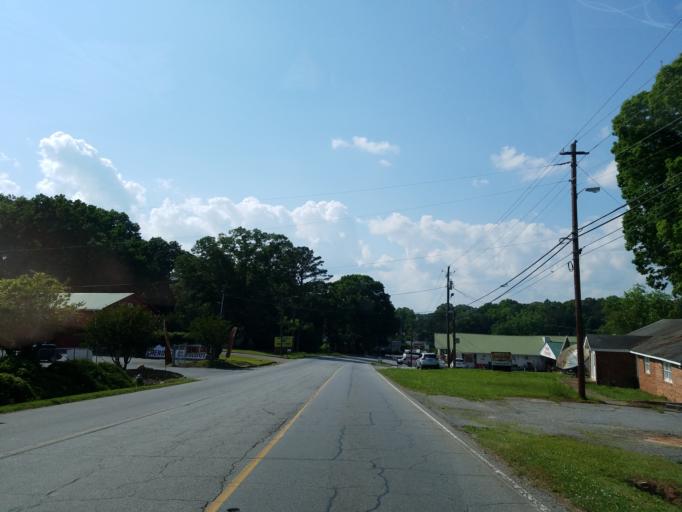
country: US
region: Georgia
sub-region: Cherokee County
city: Canton
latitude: 34.2177
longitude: -84.5058
